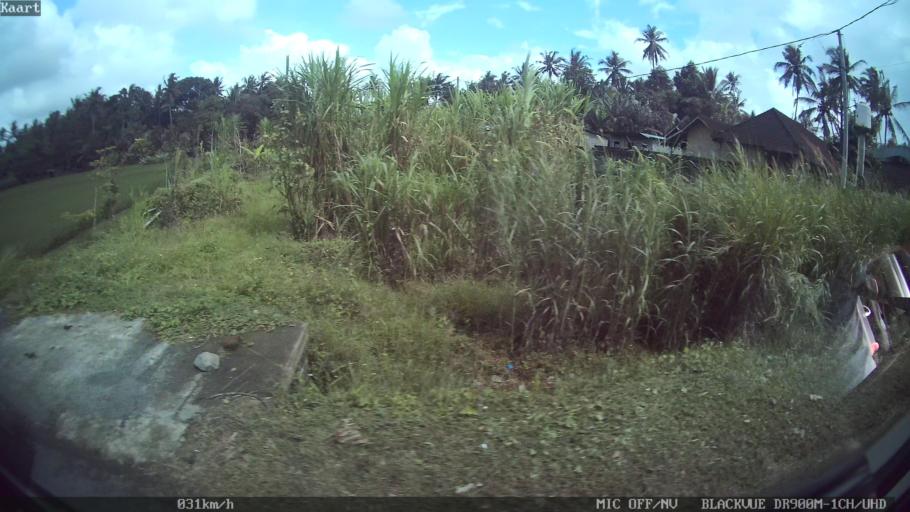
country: ID
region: Bali
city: Banjar Bucu
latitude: -8.5741
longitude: 115.2031
